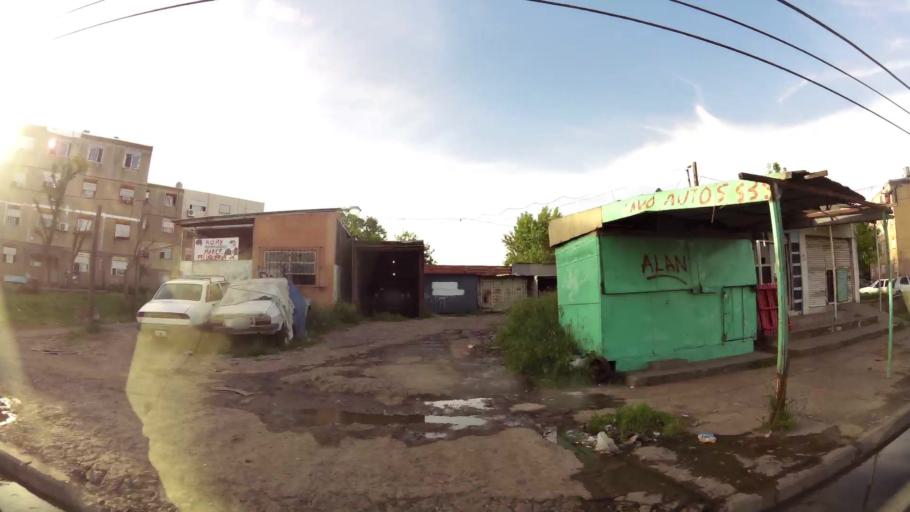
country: AR
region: Buenos Aires
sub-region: Partido de Almirante Brown
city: Adrogue
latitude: -34.8207
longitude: -58.3405
